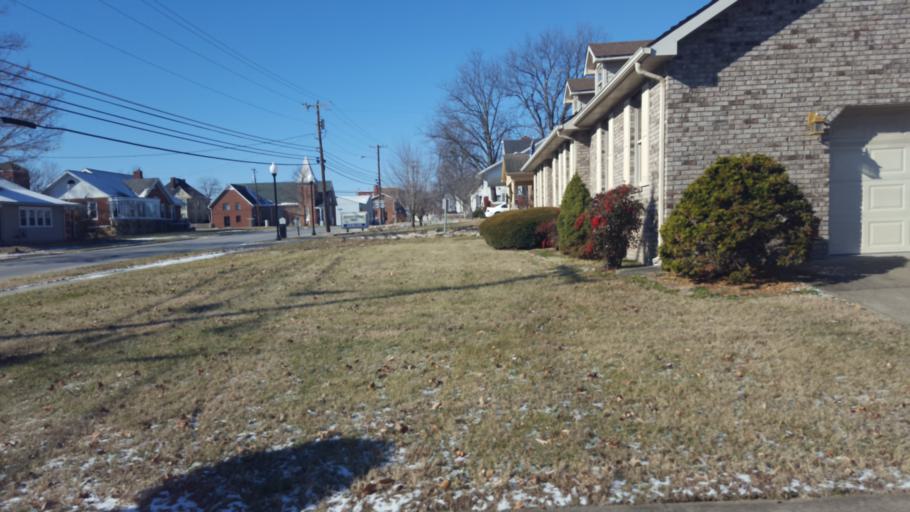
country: US
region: Kentucky
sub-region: Crittenden County
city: Marion
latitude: 37.3329
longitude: -88.0782
